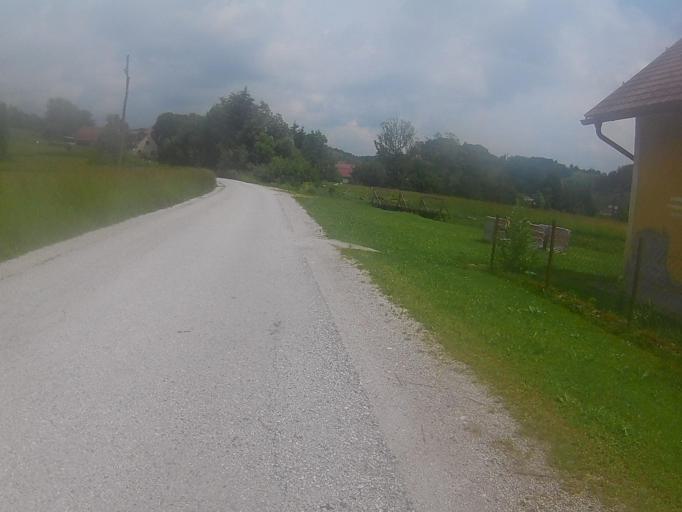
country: SI
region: Kungota
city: Zgornja Kungota
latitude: 46.6355
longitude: 15.6114
